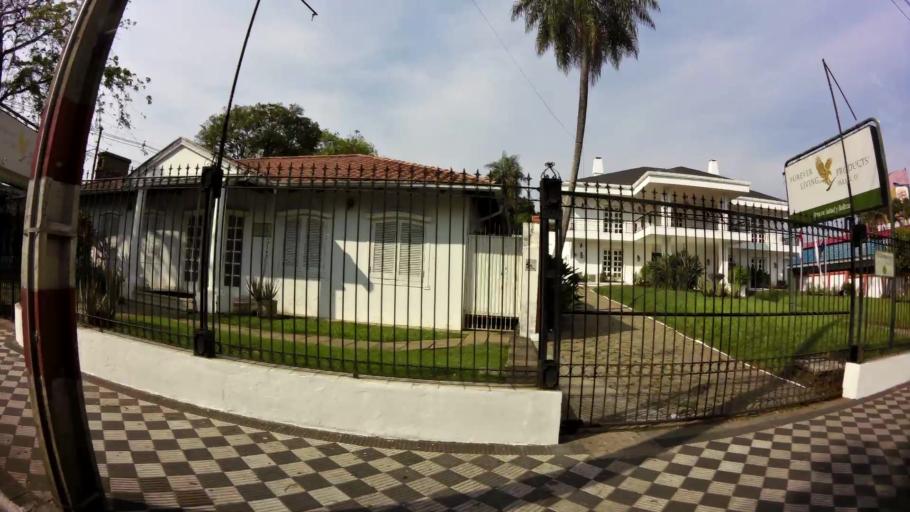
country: PY
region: Central
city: Lambare
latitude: -25.2984
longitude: -57.5699
